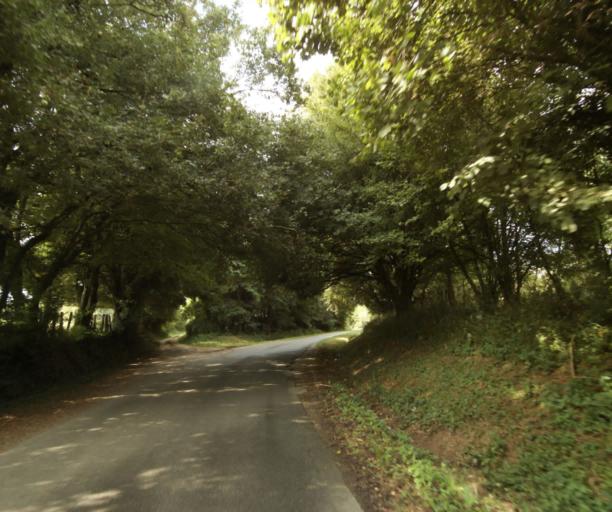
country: FR
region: Bourgogne
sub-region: Departement de Saone-et-Loire
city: Tournus
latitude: 46.5501
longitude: 4.9143
